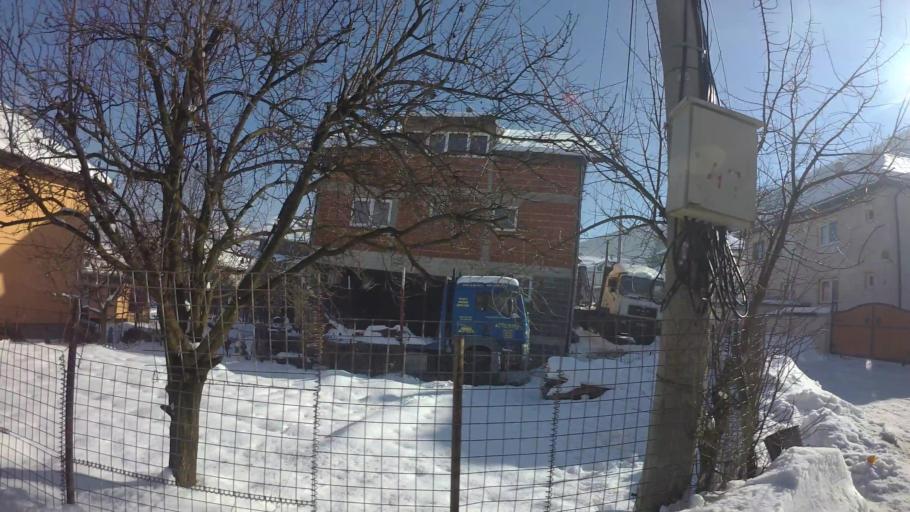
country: BA
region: Federation of Bosnia and Herzegovina
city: Gracanica
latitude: 43.7919
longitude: 18.3163
